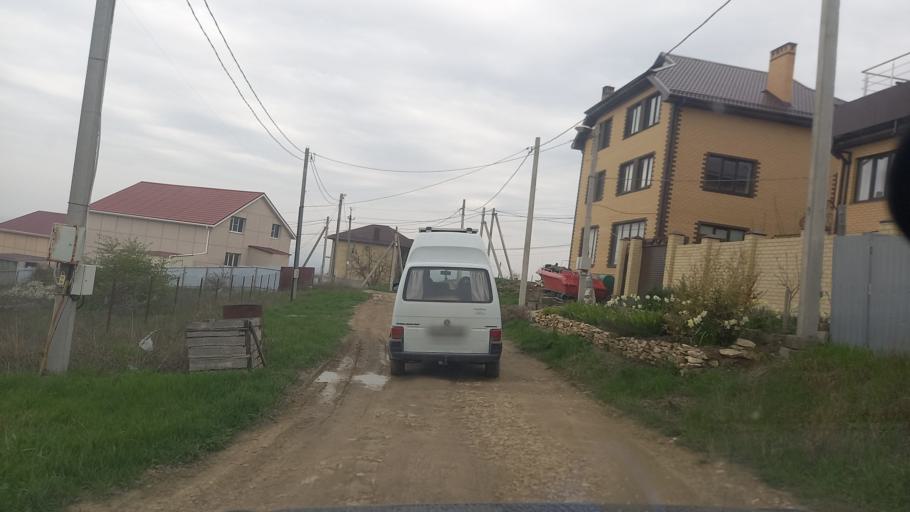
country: RU
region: Krasnodarskiy
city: Anapa
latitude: 44.8565
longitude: 37.3421
